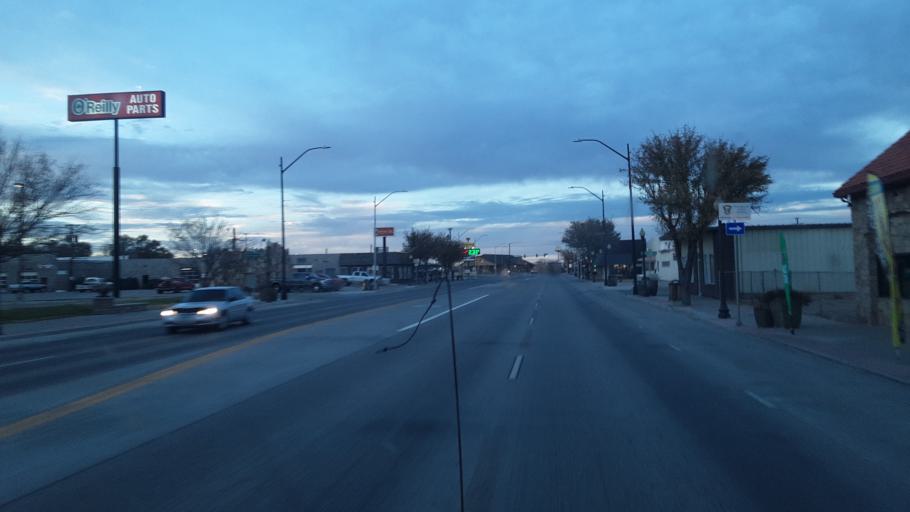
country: US
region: Colorado
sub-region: Prowers County
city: Lamar
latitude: 38.0938
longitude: -102.6196
